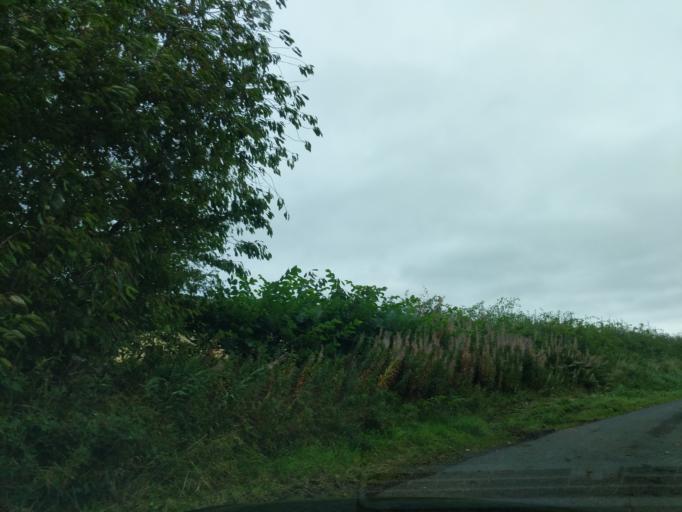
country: GB
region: Scotland
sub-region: The Scottish Borders
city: Saint Boswells
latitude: 55.5876
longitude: -2.6182
